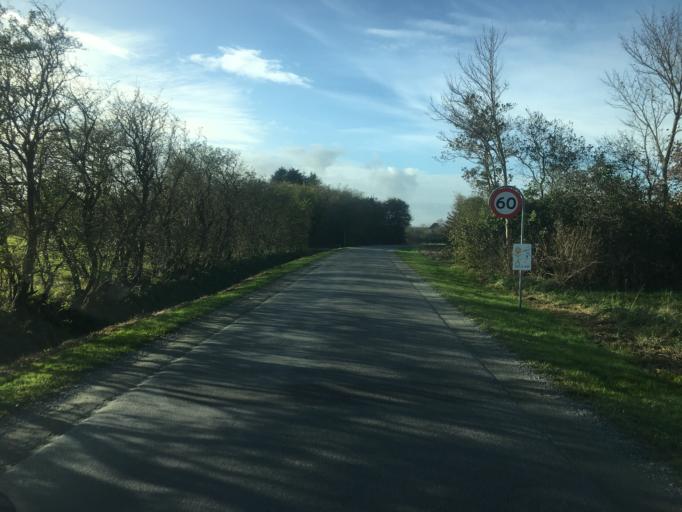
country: DK
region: South Denmark
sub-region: Tonder Kommune
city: Logumkloster
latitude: 55.0737
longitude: 8.9414
